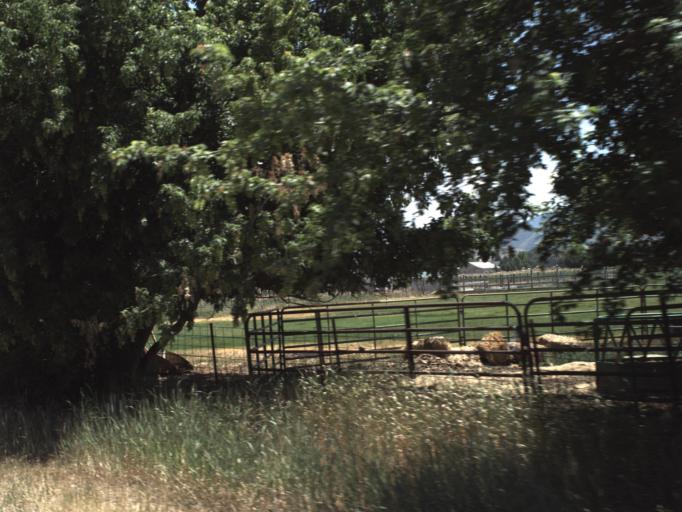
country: US
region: Utah
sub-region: Weber County
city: Wolf Creek
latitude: 41.2621
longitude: -111.7446
